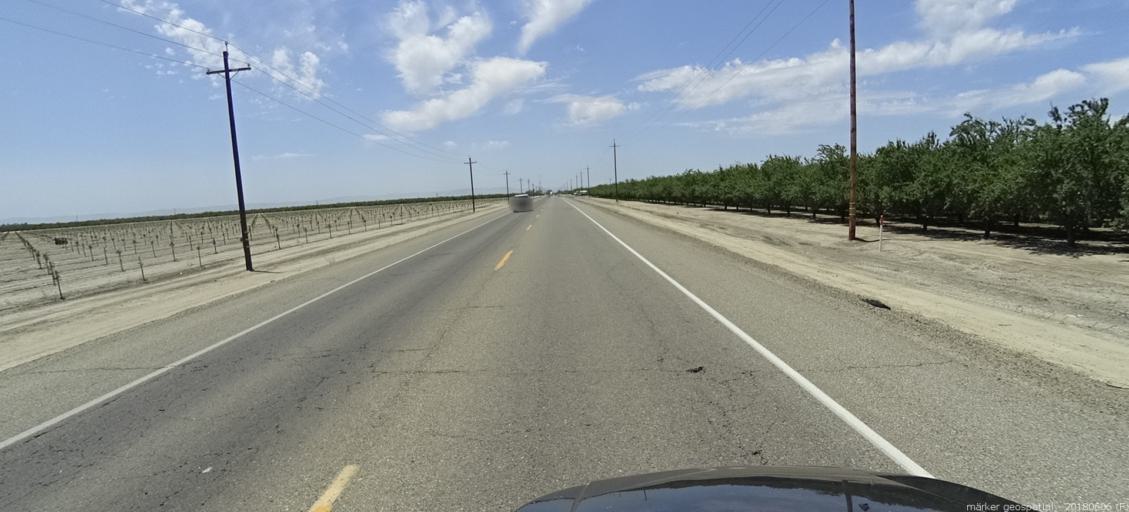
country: US
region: California
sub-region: Fresno County
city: Firebaugh
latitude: 36.8585
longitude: -120.3781
